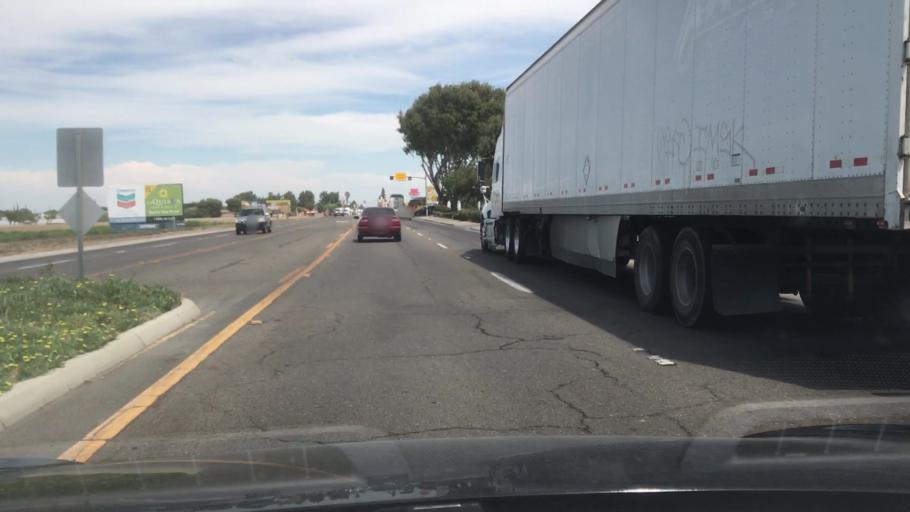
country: US
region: California
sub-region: Merced County
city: Los Banos
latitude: 37.0568
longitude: -120.8699
